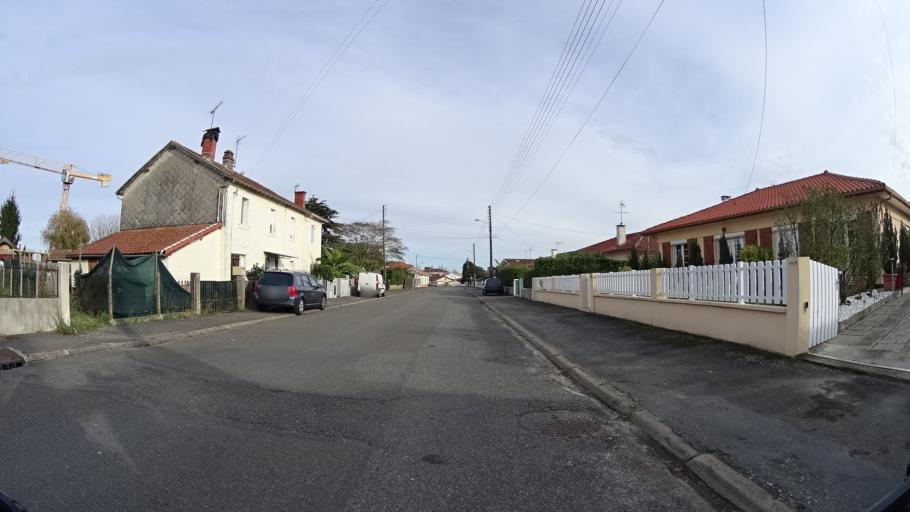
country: FR
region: Aquitaine
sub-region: Departement des Landes
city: Saint-Paul-les-Dax
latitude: 43.7310
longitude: -1.0536
